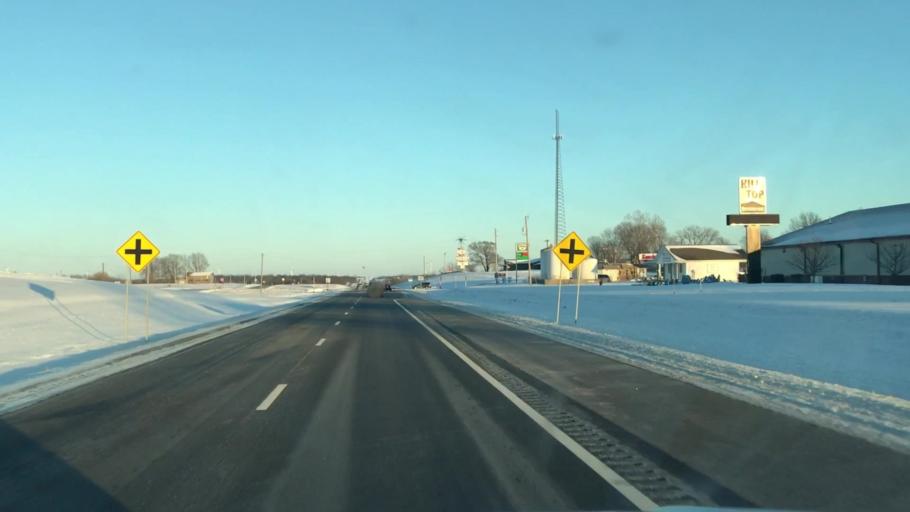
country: US
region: Missouri
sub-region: Clinton County
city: Gower
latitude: 39.7620
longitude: -94.5000
